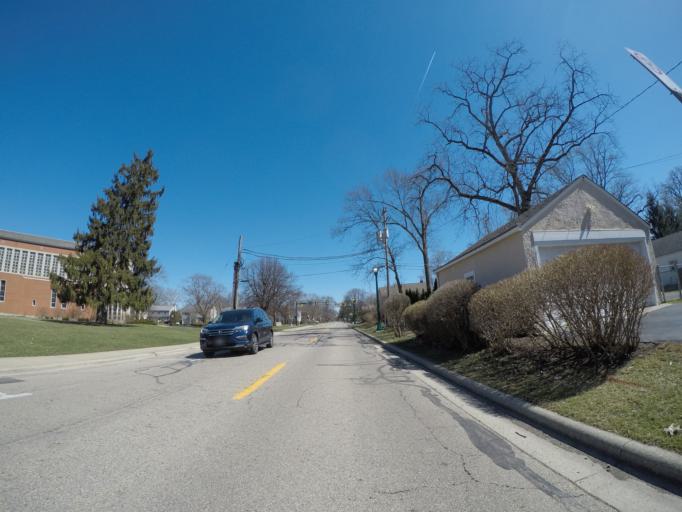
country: US
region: Ohio
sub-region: Franklin County
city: Upper Arlington
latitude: 40.0120
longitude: -83.0612
